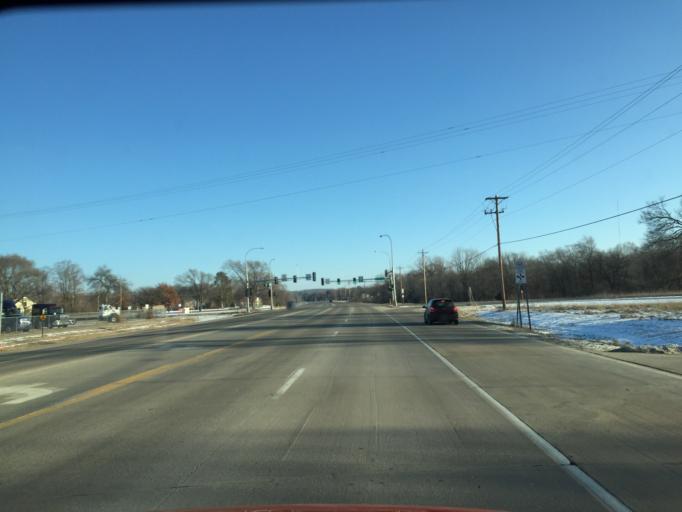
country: US
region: Minnesota
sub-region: Olmsted County
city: Rochester
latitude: 43.9931
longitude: -92.4231
